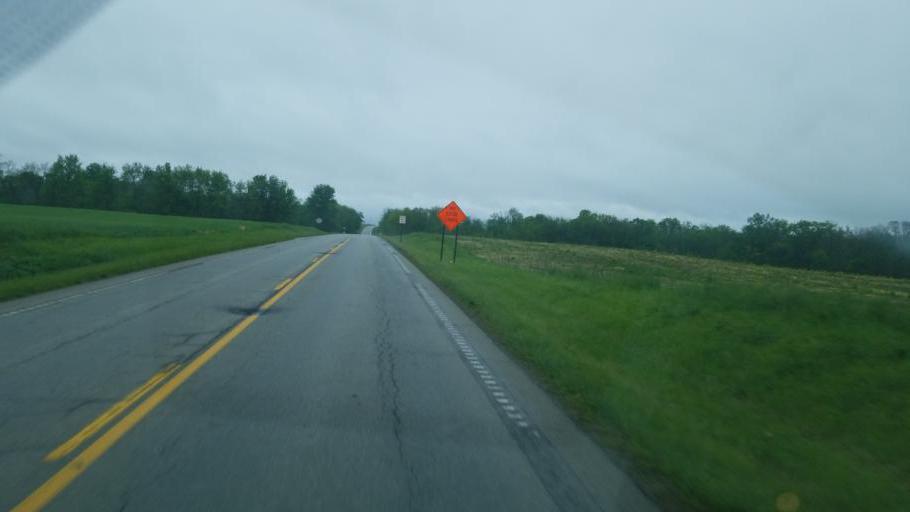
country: US
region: Ohio
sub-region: Highland County
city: Leesburg
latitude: 39.2986
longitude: -83.5840
